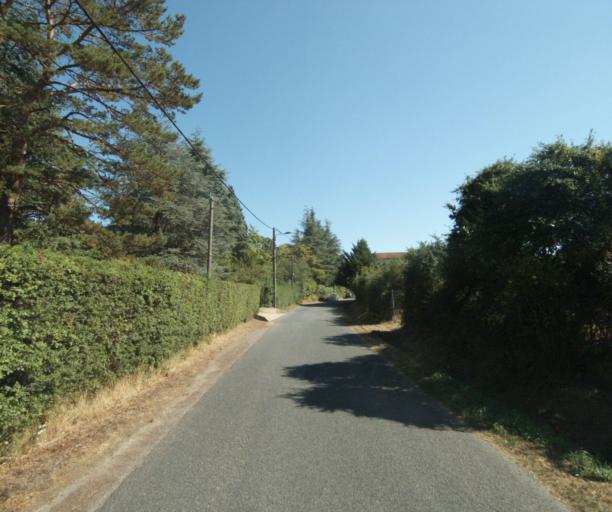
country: FR
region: Rhone-Alpes
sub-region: Departement du Rhone
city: Lozanne
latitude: 45.8379
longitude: 4.7056
